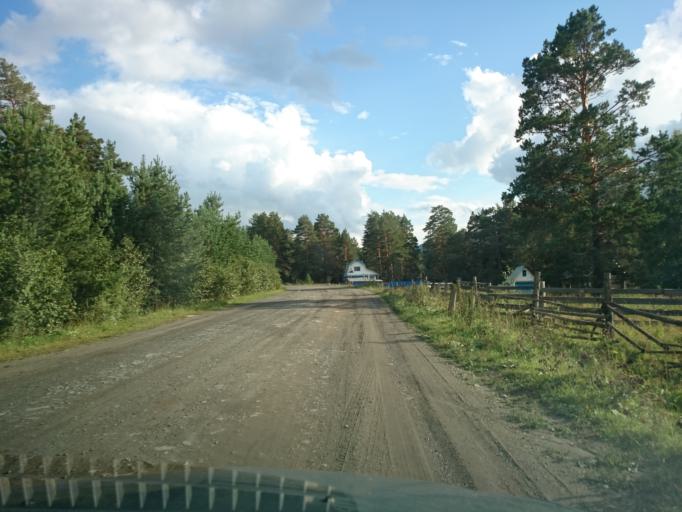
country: RU
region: Bashkortostan
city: Beloretsk
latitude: 54.0441
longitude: 58.3305
